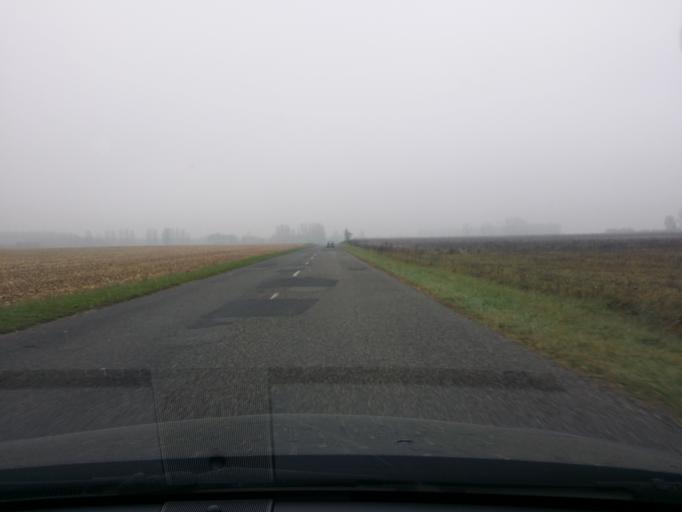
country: HU
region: Szabolcs-Szatmar-Bereg
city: Nyirbogdany
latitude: 48.0527
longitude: 21.8613
